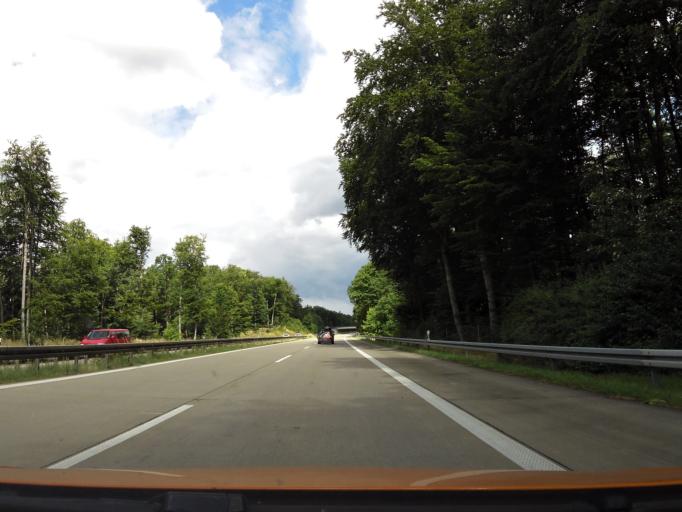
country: DE
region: Brandenburg
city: Gerswalde
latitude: 53.1061
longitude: 13.8565
